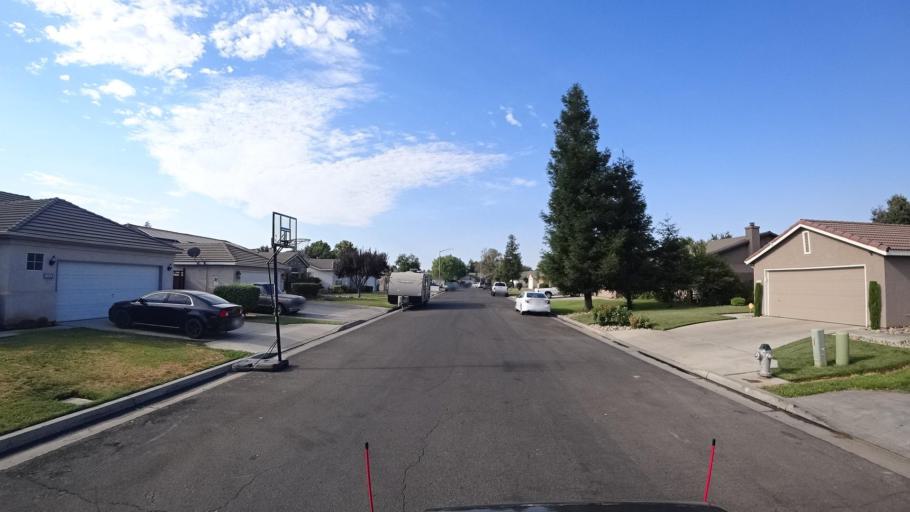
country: US
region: California
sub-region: Fresno County
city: Sunnyside
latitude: 36.7138
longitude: -119.6992
